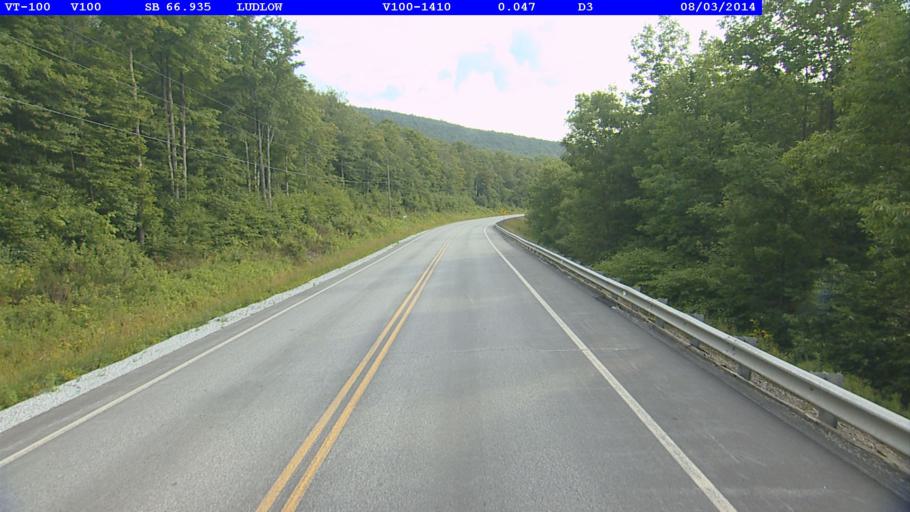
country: US
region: Vermont
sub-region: Windsor County
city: Chester
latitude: 43.3529
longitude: -72.7559
